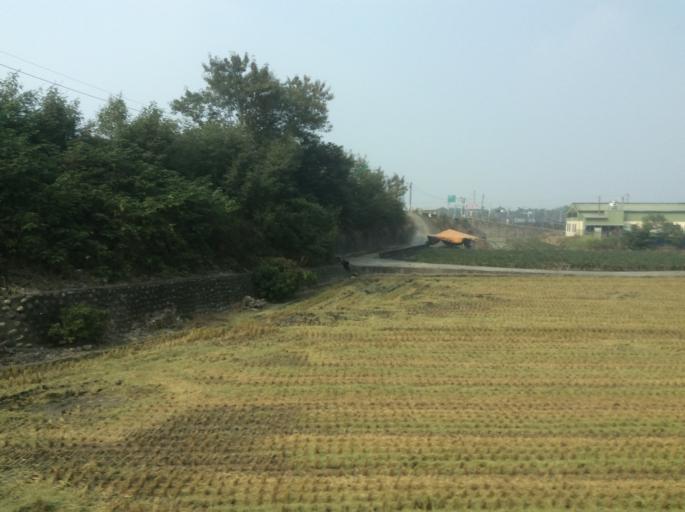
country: TW
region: Taiwan
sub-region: Yunlin
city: Douliu
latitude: 23.7700
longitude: 120.6321
